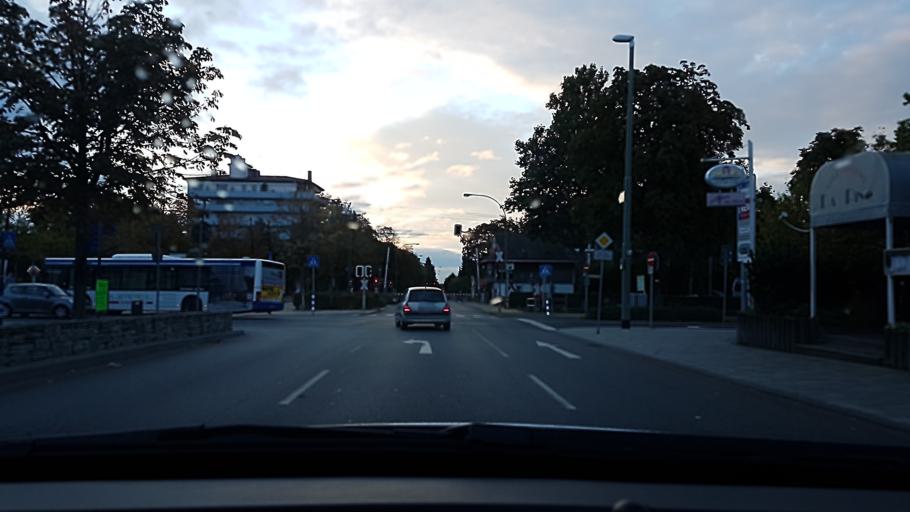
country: DE
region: Hesse
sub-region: Regierungsbezirk Darmstadt
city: Oberursel
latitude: 50.1988
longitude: 8.5858
